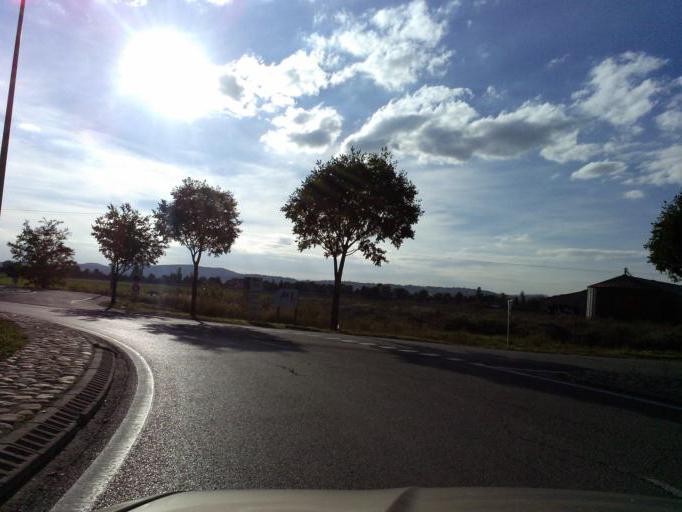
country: FR
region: Provence-Alpes-Cote d'Azur
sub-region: Departement des Alpes-de-Haute-Provence
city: Manosque
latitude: 43.8100
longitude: 5.8120
